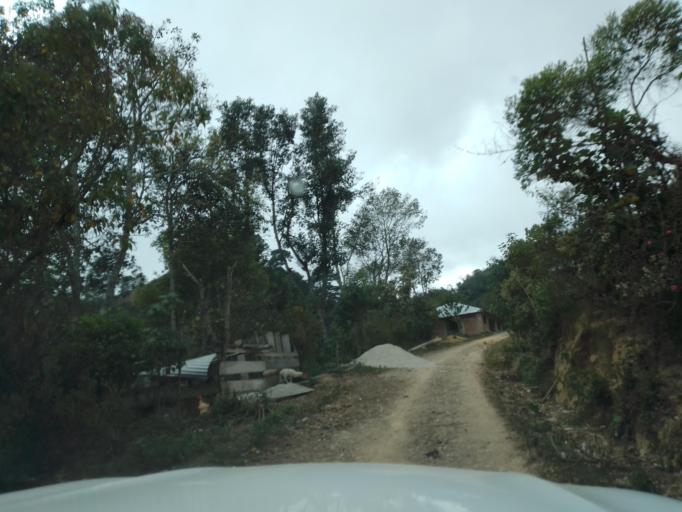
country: GT
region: San Marcos
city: Tacana
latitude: 15.2192
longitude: -92.2117
